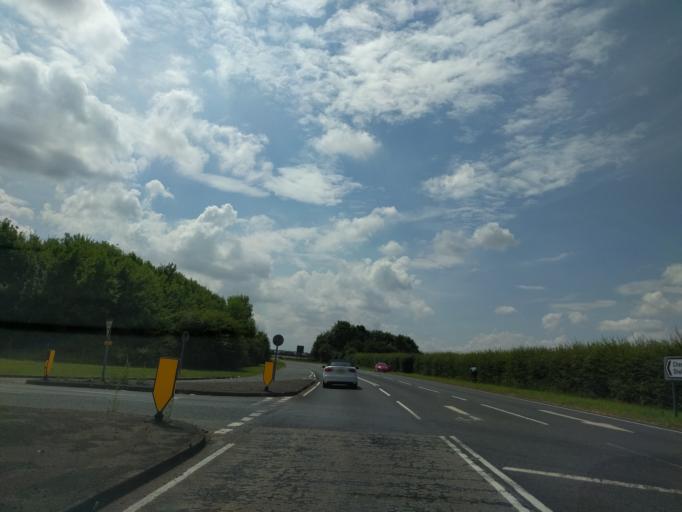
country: GB
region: England
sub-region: Cambridgeshire
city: Fulbourn
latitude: 52.2053
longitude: 0.1853
